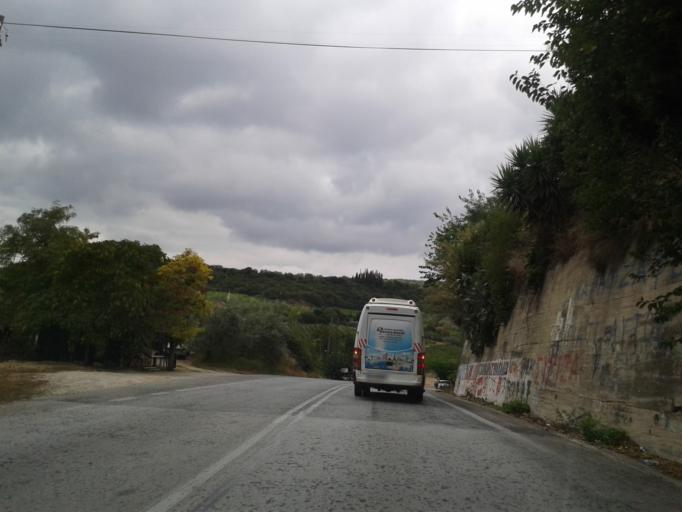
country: GR
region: Peloponnese
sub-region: Nomos Korinthias
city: Nemea
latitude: 37.7835
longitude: 22.7206
